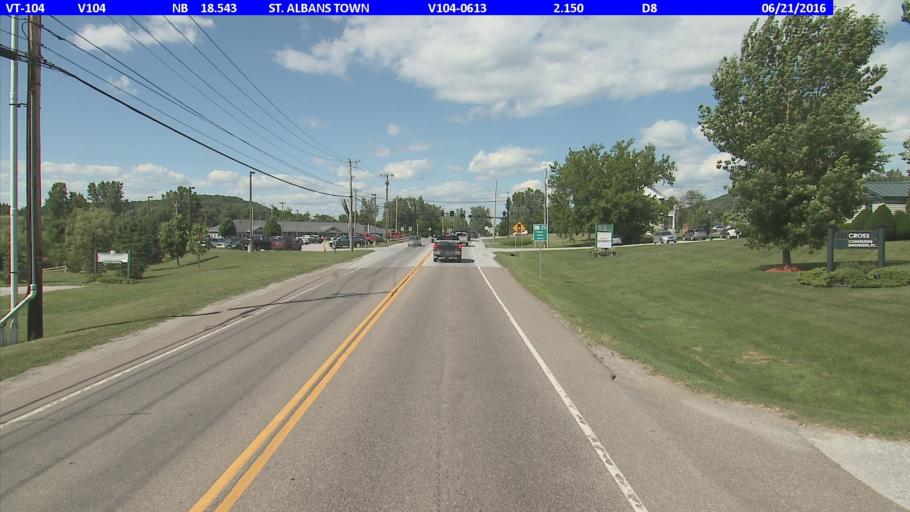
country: US
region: Vermont
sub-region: Franklin County
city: Saint Albans
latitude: 44.8037
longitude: -73.0695
